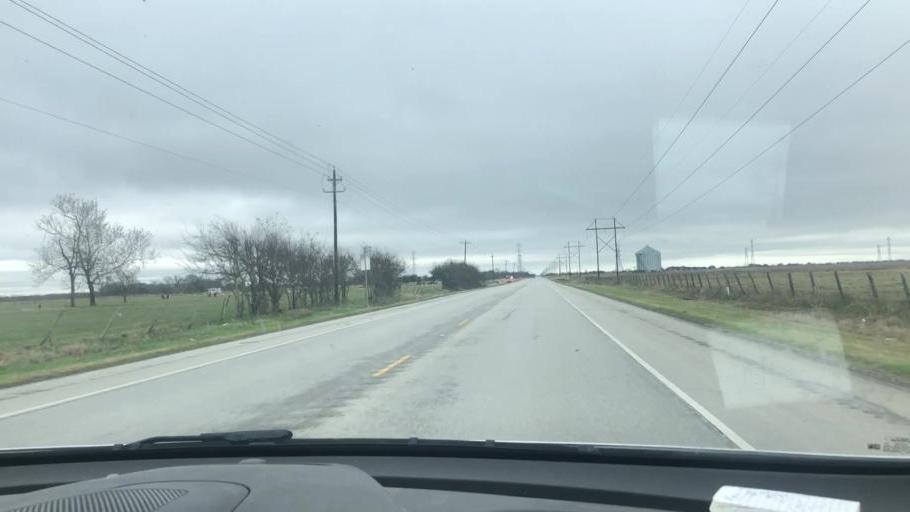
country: US
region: Texas
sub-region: Wharton County
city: Boling
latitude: 29.1840
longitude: -96.0095
